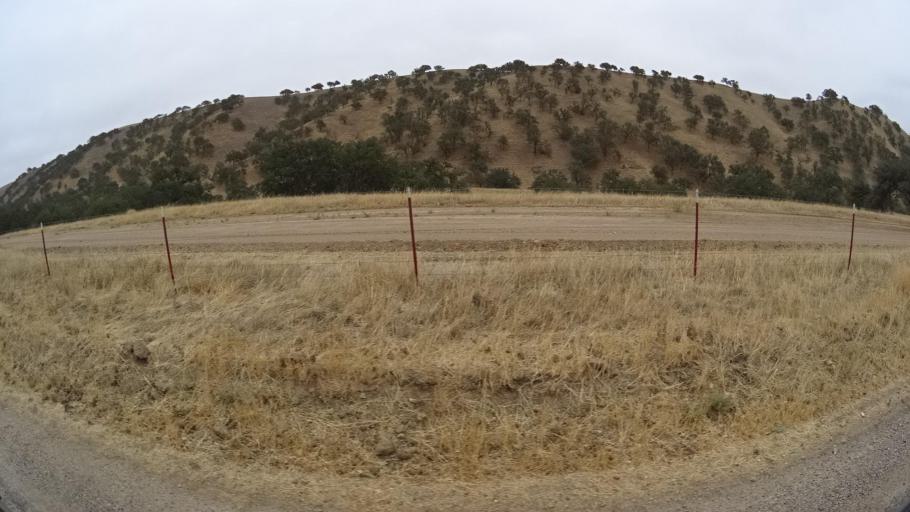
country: US
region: California
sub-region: San Luis Obispo County
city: San Miguel
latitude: 35.8668
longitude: -120.7615
